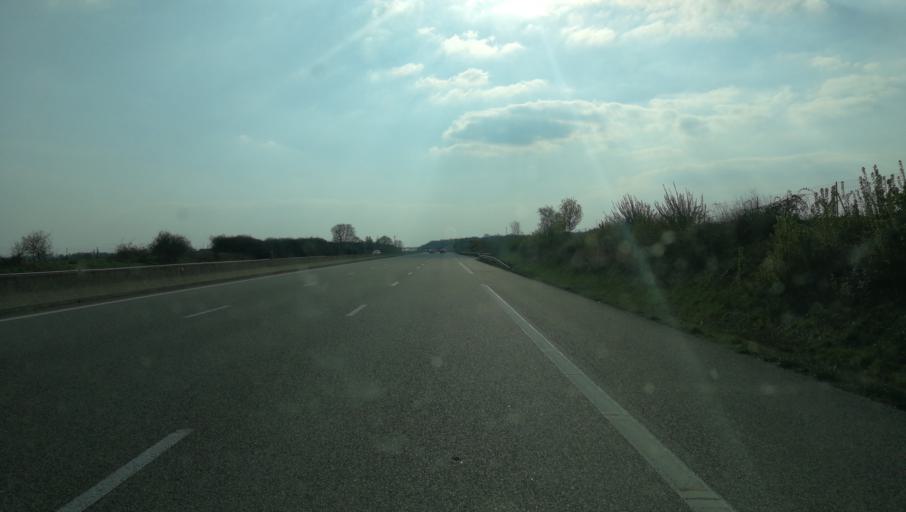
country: FR
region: Ile-de-France
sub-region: Departement des Yvelines
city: Ablis
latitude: 48.5320
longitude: 1.8581
